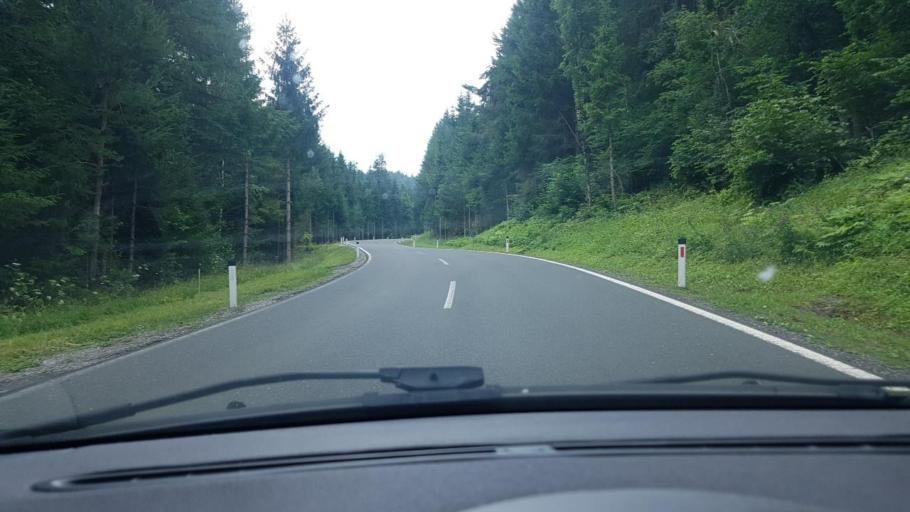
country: AT
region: Carinthia
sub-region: Politischer Bezirk Spittal an der Drau
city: Steinfeld
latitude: 46.7304
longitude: 13.2312
